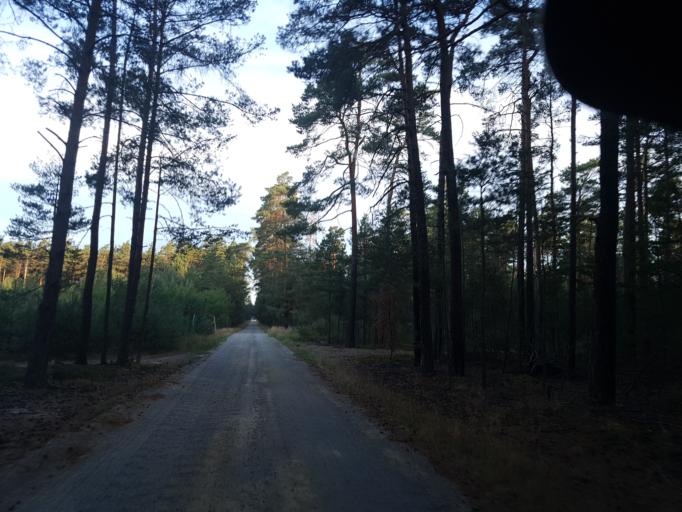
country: DE
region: Brandenburg
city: Schonewalde
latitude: 51.7407
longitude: 13.5755
